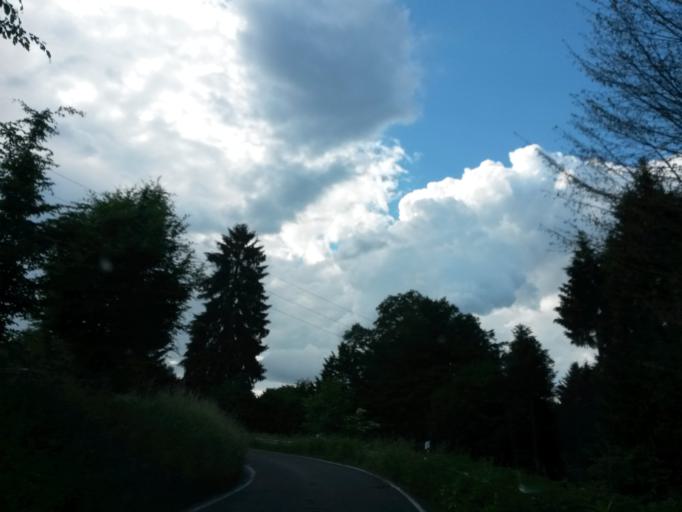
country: DE
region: North Rhine-Westphalia
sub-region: Regierungsbezirk Koln
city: Overath
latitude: 50.8900
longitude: 7.2964
